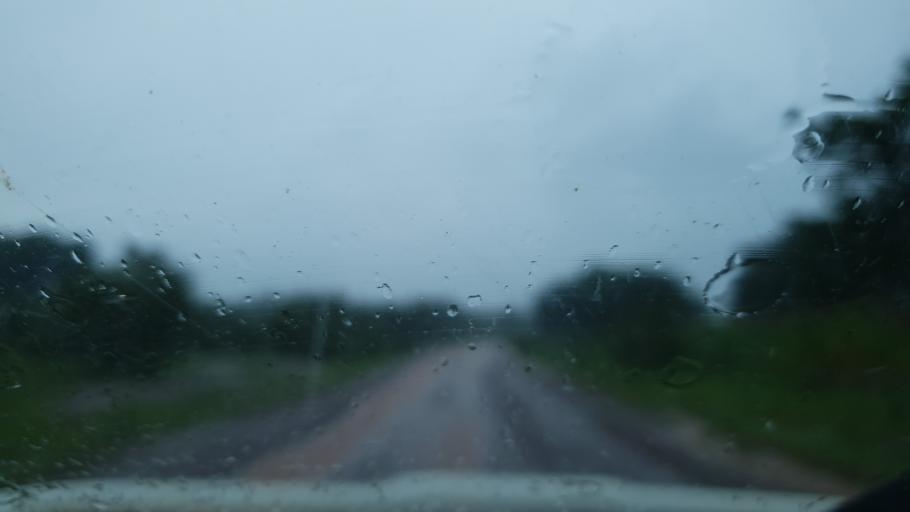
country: ML
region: Sikasso
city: Kolondieba
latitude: 11.6141
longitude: -6.6766
